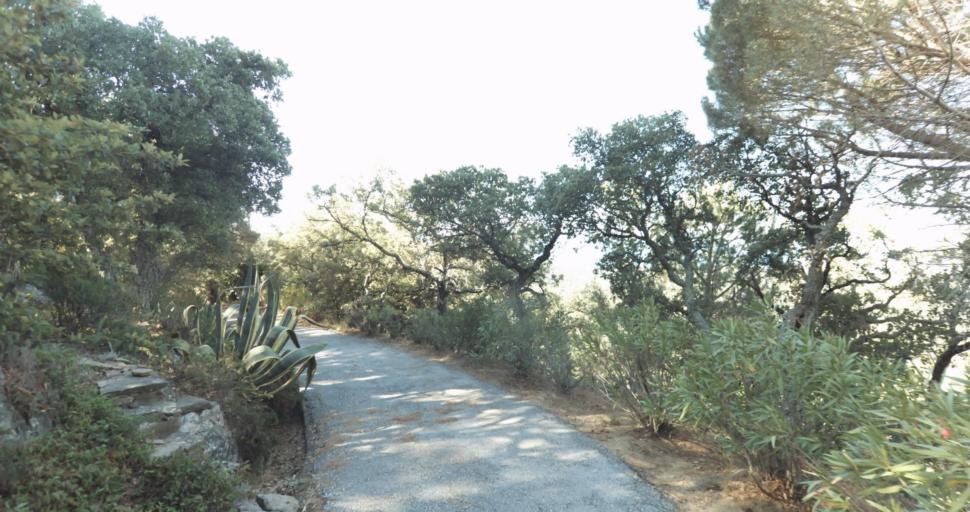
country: FR
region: Provence-Alpes-Cote d'Azur
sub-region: Departement du Var
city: Ramatuelle
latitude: 43.2179
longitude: 6.6007
